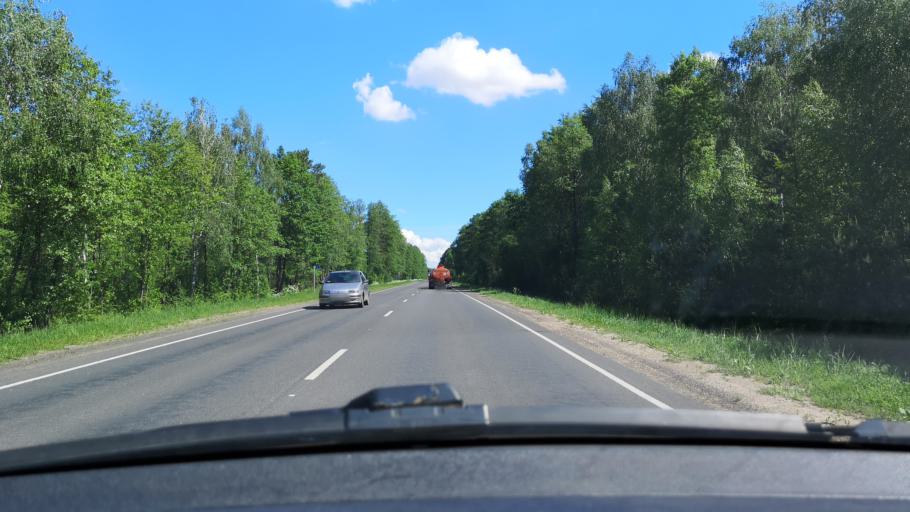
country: BY
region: Brest
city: Brest
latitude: 52.0092
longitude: 23.7208
